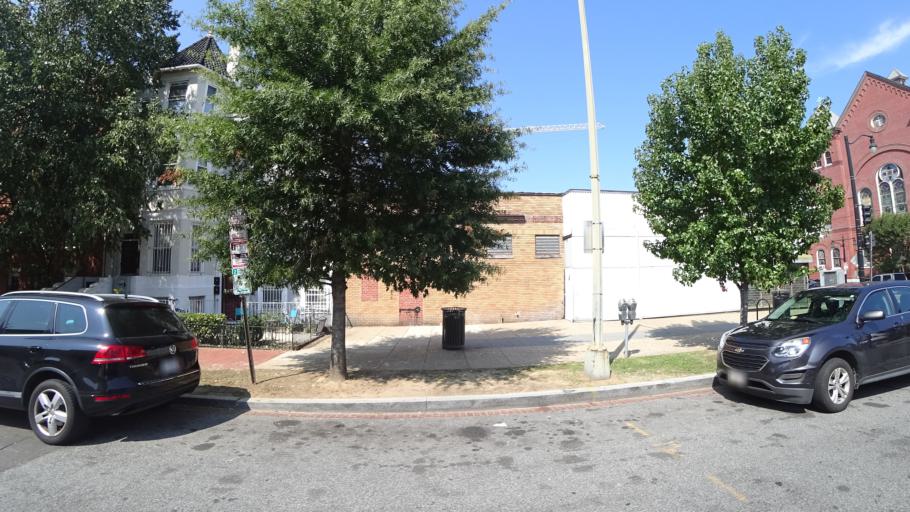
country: US
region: Washington, D.C.
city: Washington, D.C.
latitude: 38.8999
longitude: -76.9915
